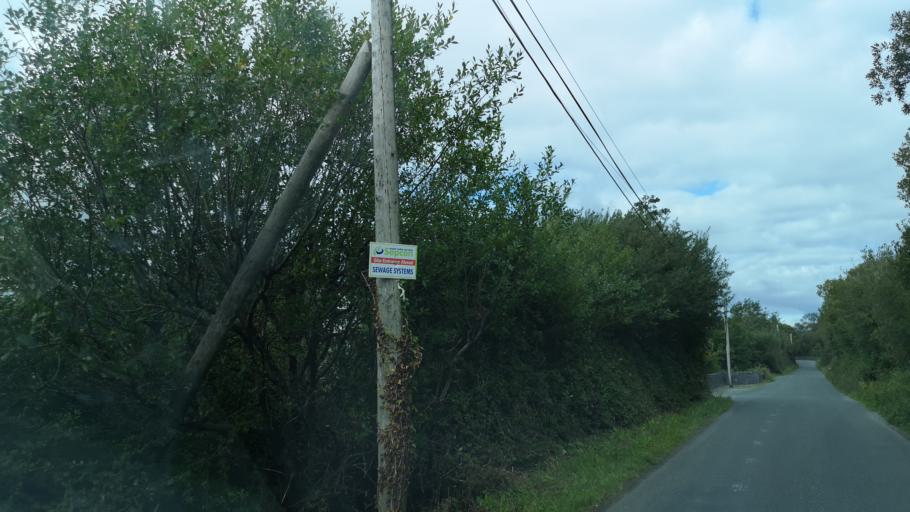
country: IE
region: Connaught
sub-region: County Galway
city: Moycullen
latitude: 53.3192
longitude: -9.1478
